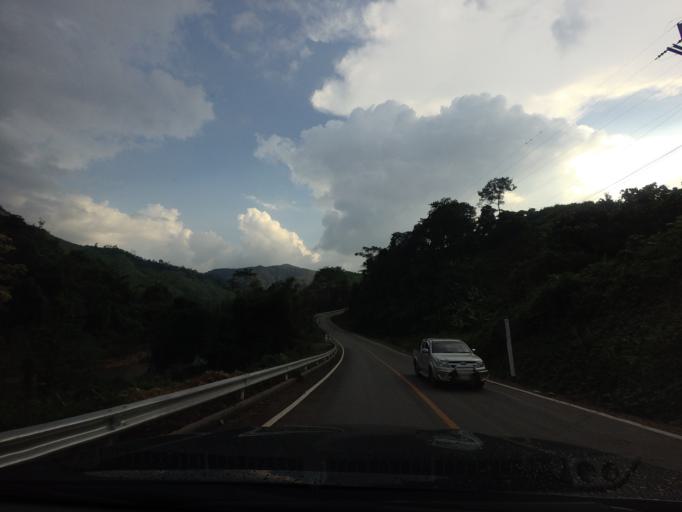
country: TH
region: Nan
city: Bo Kluea
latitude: 19.2082
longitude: 101.1856
